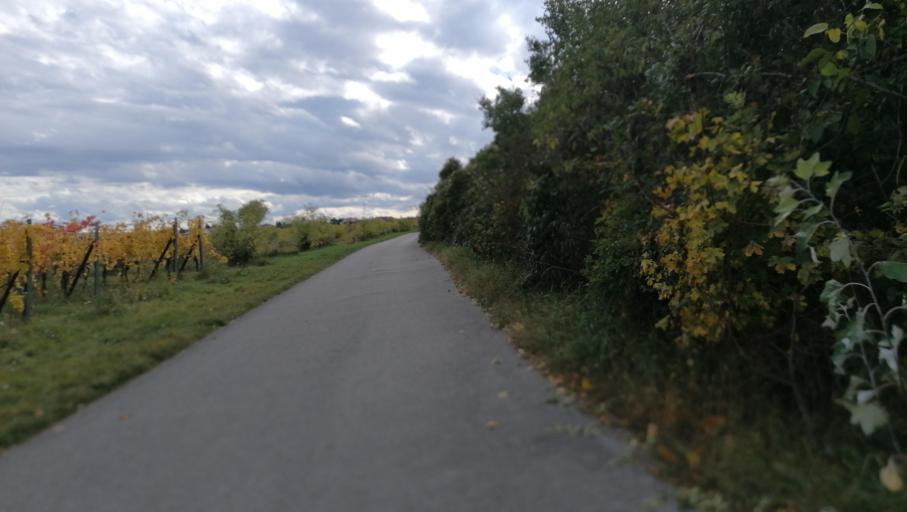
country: AT
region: Lower Austria
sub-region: Politischer Bezirk Baden
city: Tattendorf
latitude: 47.9560
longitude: 16.3089
